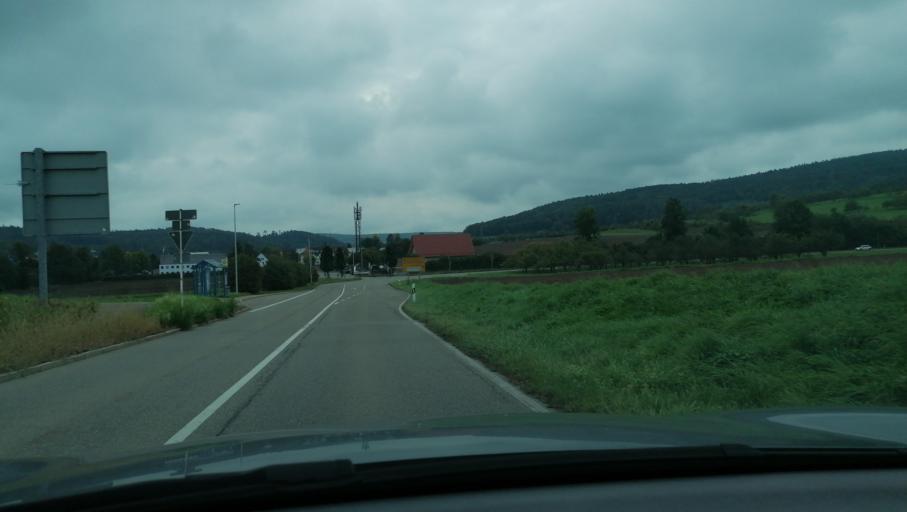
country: DE
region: Baden-Wuerttemberg
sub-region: Regierungsbezirk Stuttgart
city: Winnenden
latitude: 48.8694
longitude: 9.4197
